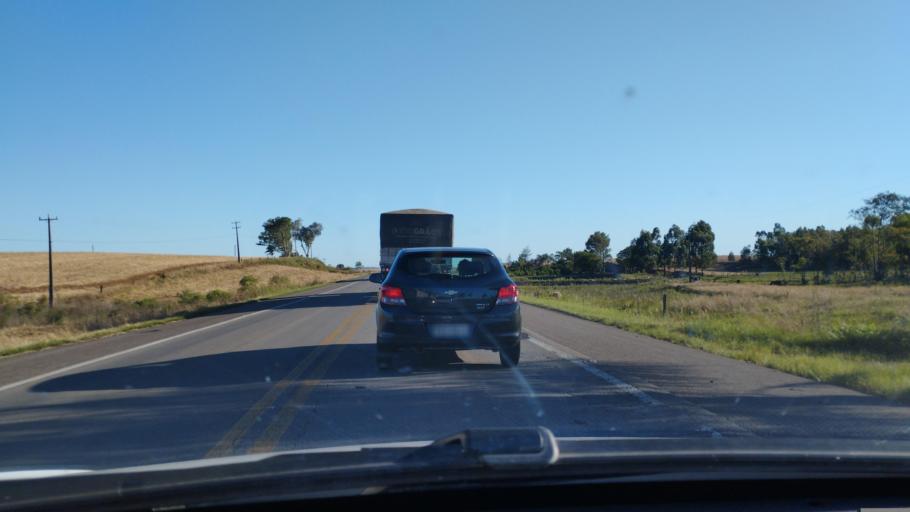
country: BR
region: Rio Grande do Sul
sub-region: Julio De Castilhos
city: Julio de Castilhos
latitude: -29.3803
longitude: -53.6704
